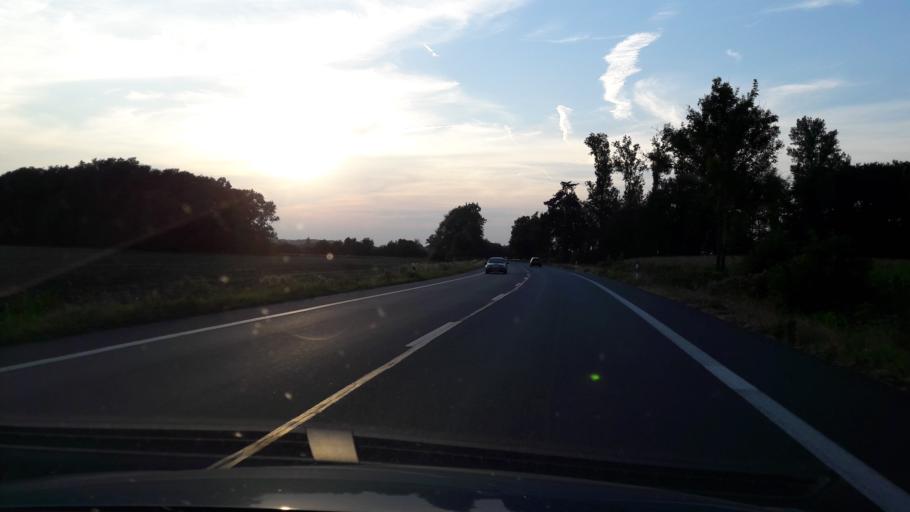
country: DE
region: North Rhine-Westphalia
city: Ahlen
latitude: 51.8257
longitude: 7.8921
